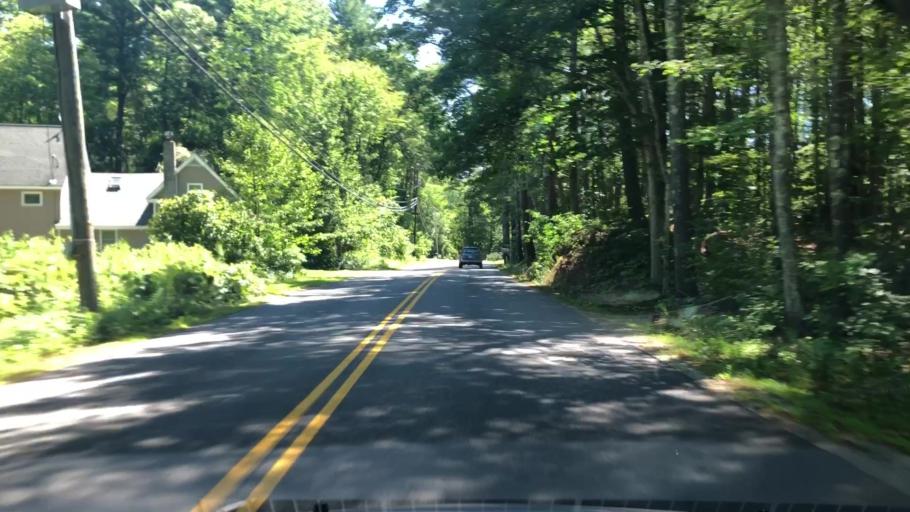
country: US
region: New Hampshire
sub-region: Hillsborough County
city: Milford
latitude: 42.8653
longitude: -71.6094
